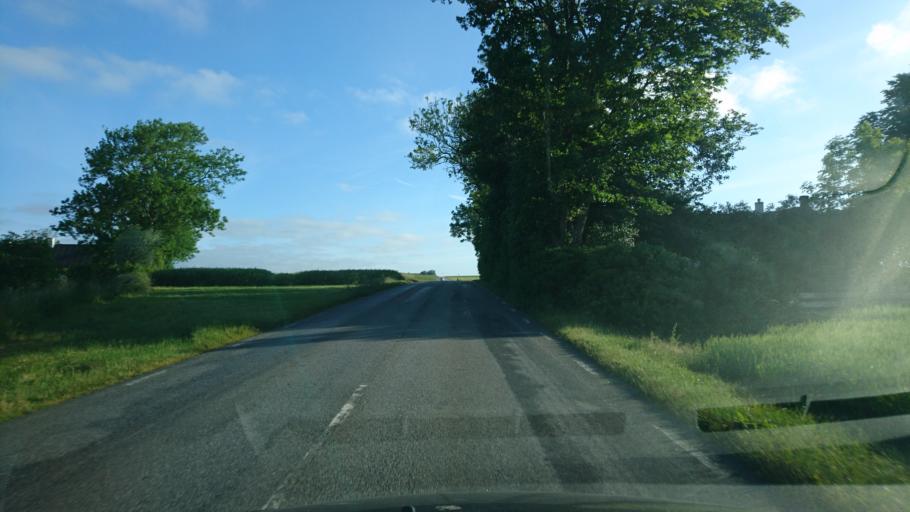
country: SE
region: Skane
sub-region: Tomelilla Kommun
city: Tomelilla
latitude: 55.4785
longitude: 14.1001
